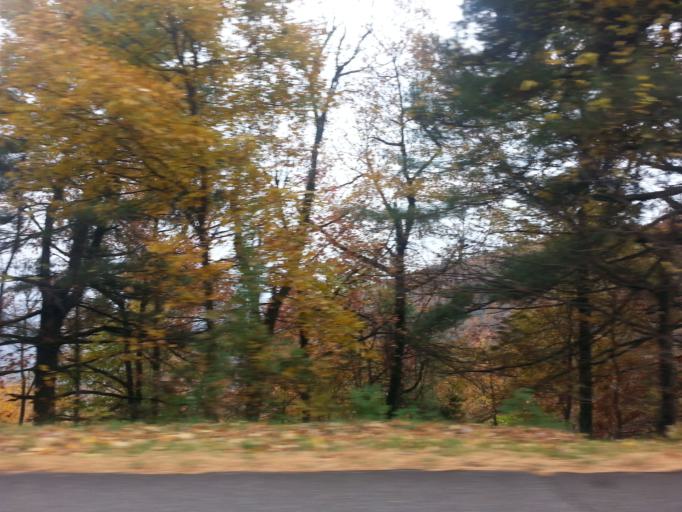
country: US
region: North Carolina
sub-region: Ashe County
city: Jefferson
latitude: 36.2926
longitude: -81.3717
